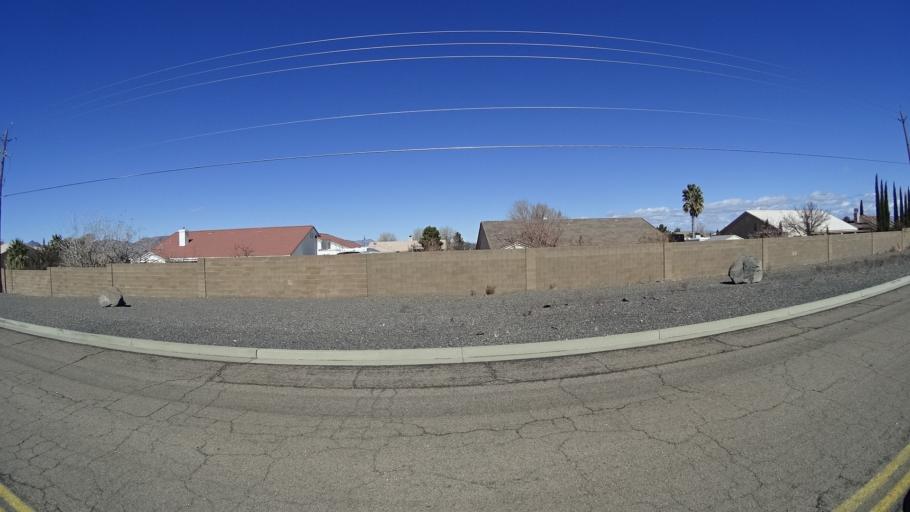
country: US
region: Arizona
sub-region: Mohave County
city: Kingman
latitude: 35.2028
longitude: -113.9729
